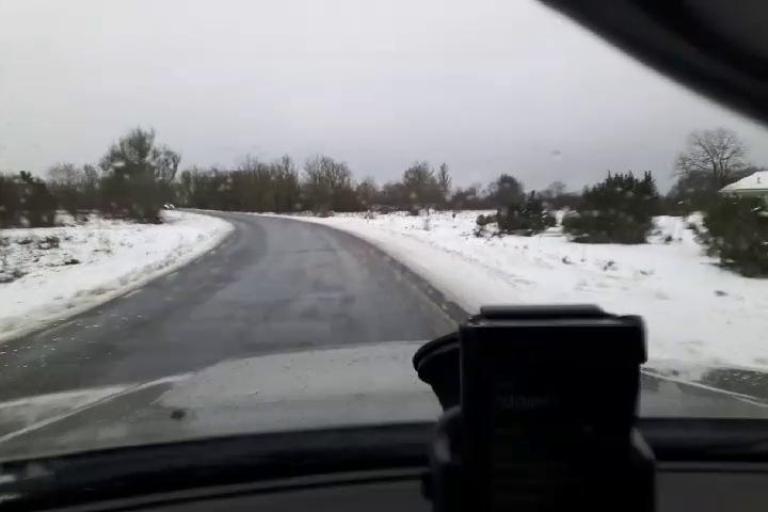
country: EE
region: Harju
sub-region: Harku vald
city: Tabasalu
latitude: 59.4246
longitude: 24.4241
